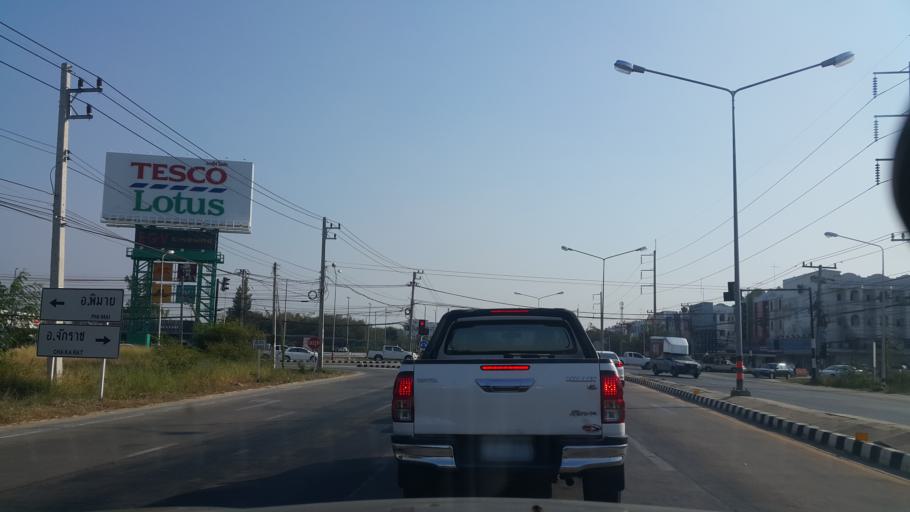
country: TH
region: Nakhon Ratchasima
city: Phimai
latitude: 15.2158
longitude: 102.4856
